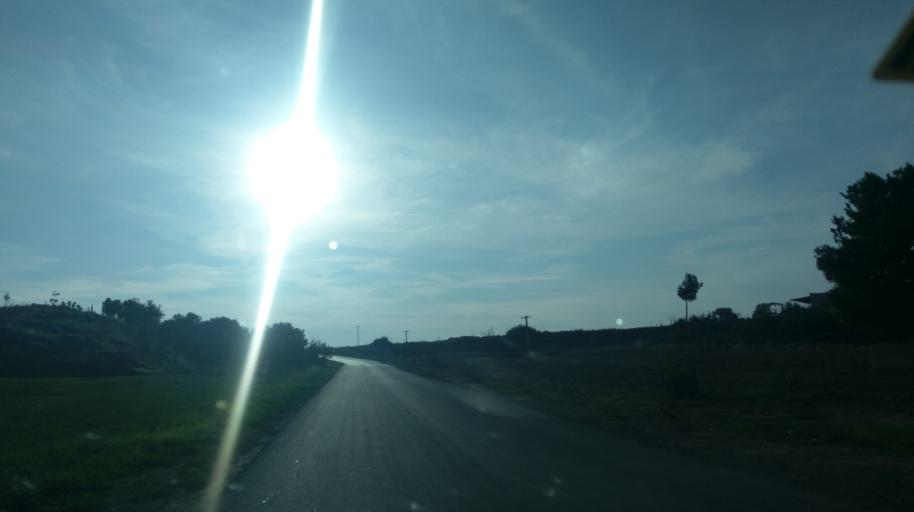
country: CY
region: Ammochostos
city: Acheritou
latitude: 35.1065
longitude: 33.8654
